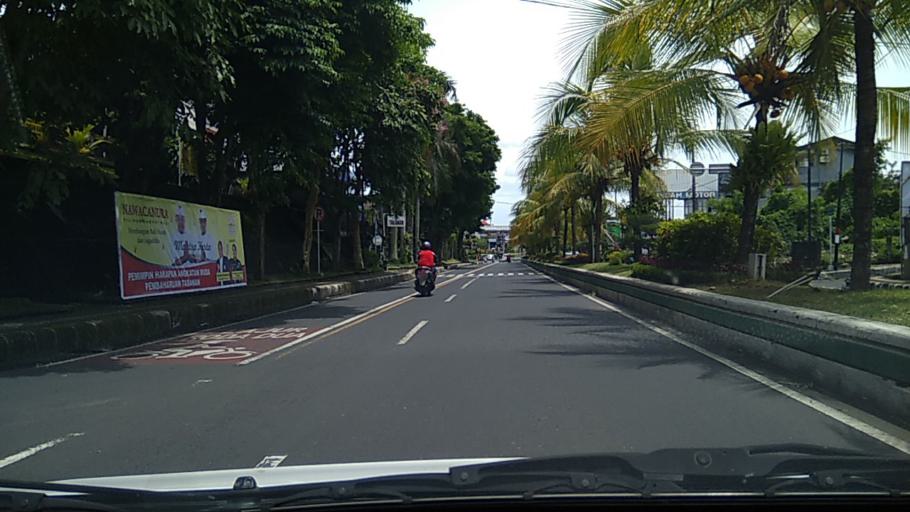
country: ID
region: Bali
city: Tabanan
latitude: -8.5399
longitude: 115.1333
